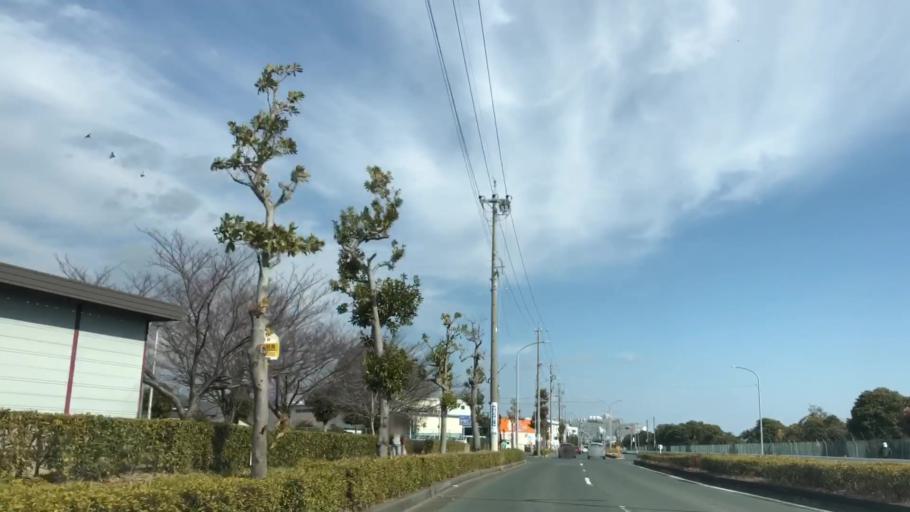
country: JP
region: Shizuoka
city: Hamamatsu
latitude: 34.7533
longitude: 137.7103
